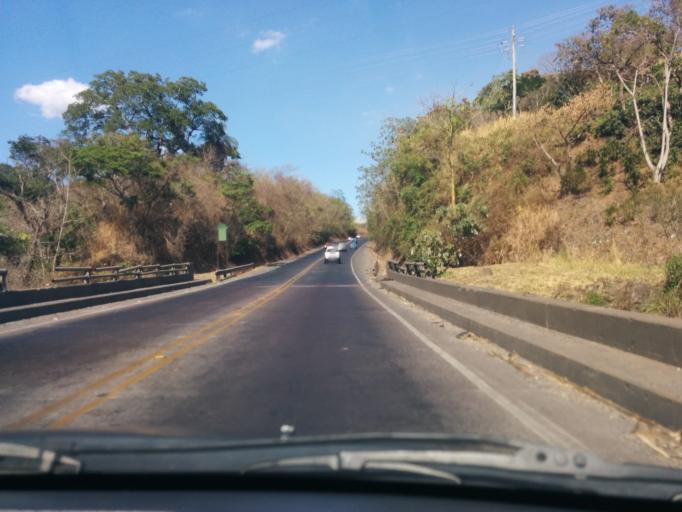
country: CR
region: Alajuela
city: Carrillos
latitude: 10.0022
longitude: -84.3106
